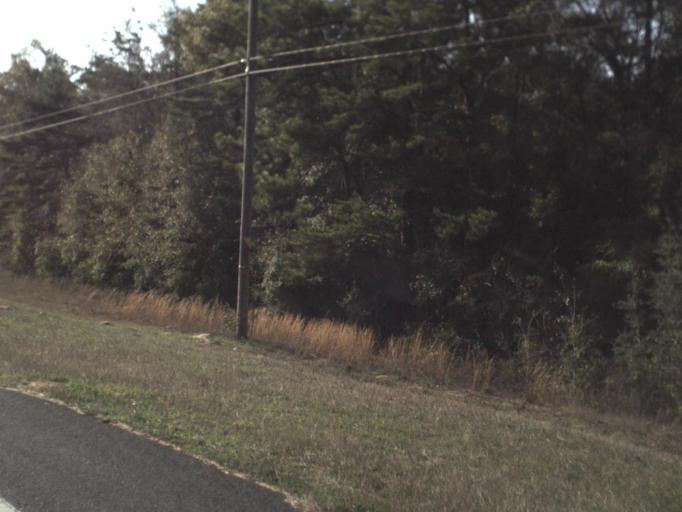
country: US
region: Florida
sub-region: Bay County
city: Youngstown
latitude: 30.4327
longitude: -85.5396
